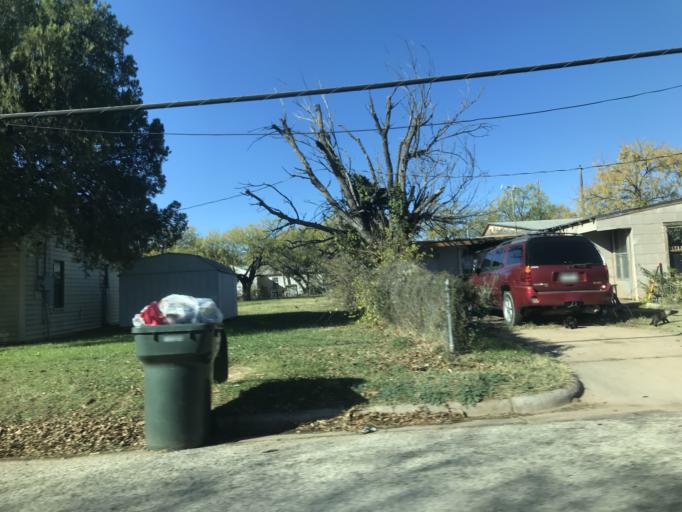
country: US
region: Texas
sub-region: Taylor County
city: Abilene
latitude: 32.4572
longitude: -99.7489
